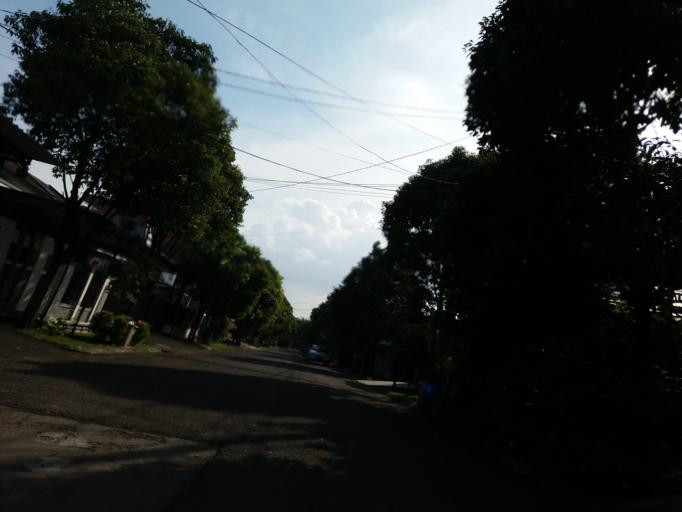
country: ID
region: West Java
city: Bandung
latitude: -6.9621
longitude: 107.6333
